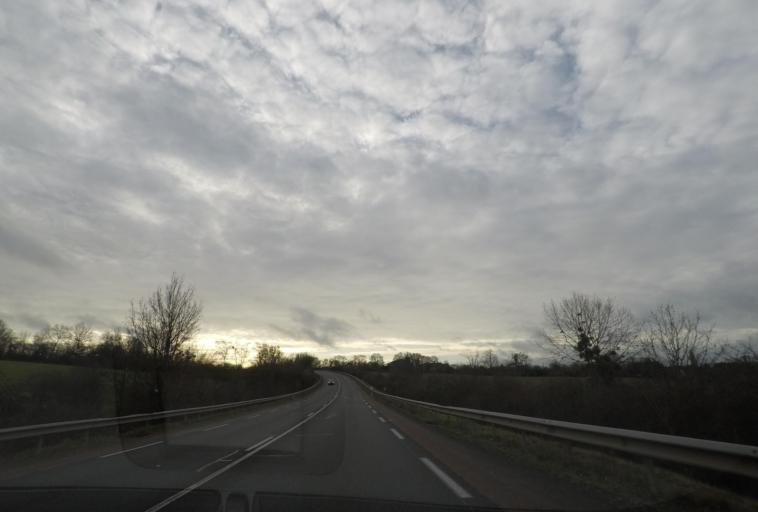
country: FR
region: Pays de la Loire
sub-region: Departement de la Sarthe
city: Saint-Calais
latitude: 47.9230
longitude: 0.7625
